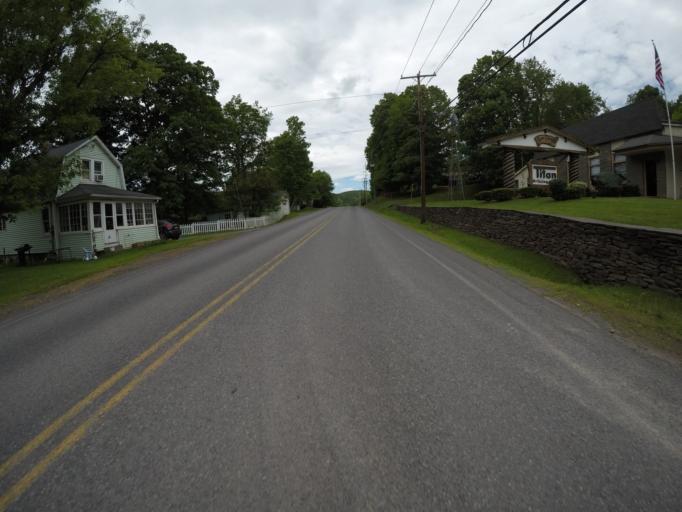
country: US
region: New York
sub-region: Delaware County
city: Stamford
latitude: 42.1515
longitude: -74.6197
